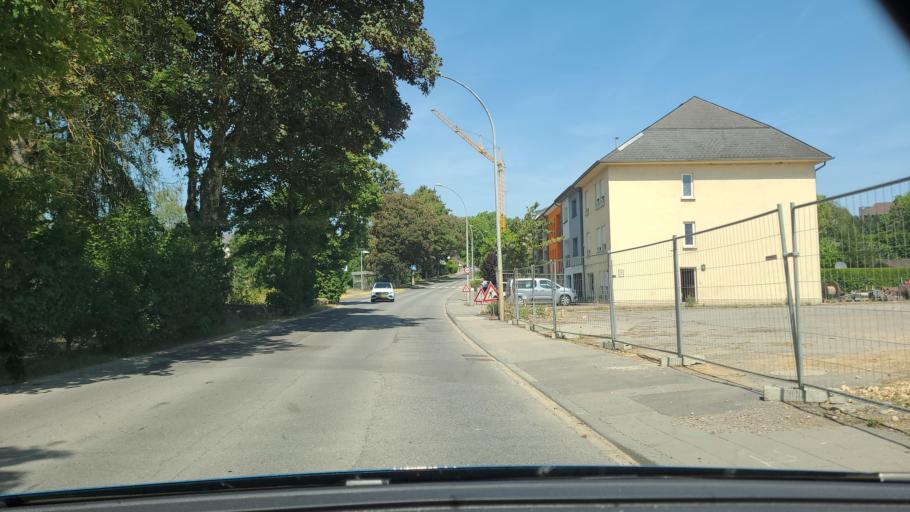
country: LU
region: Luxembourg
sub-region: Canton d'Esch-sur-Alzette
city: Sanem
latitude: 49.5431
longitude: 5.9327
